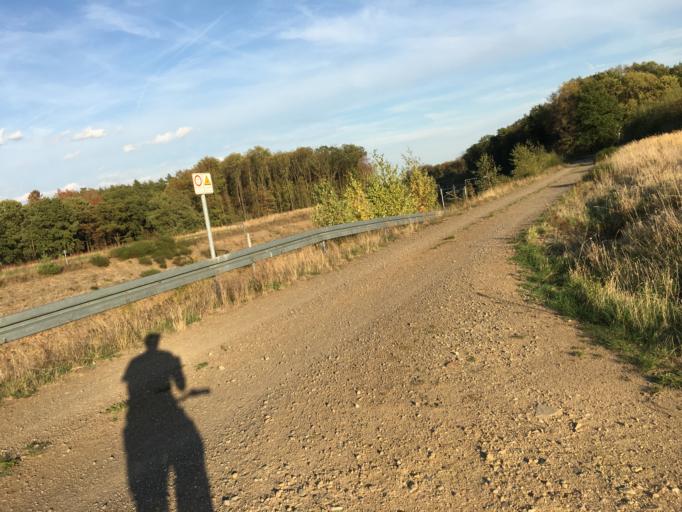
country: DE
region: North Rhine-Westphalia
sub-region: Regierungsbezirk Koln
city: Merzenich
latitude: 50.8494
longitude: 6.5258
